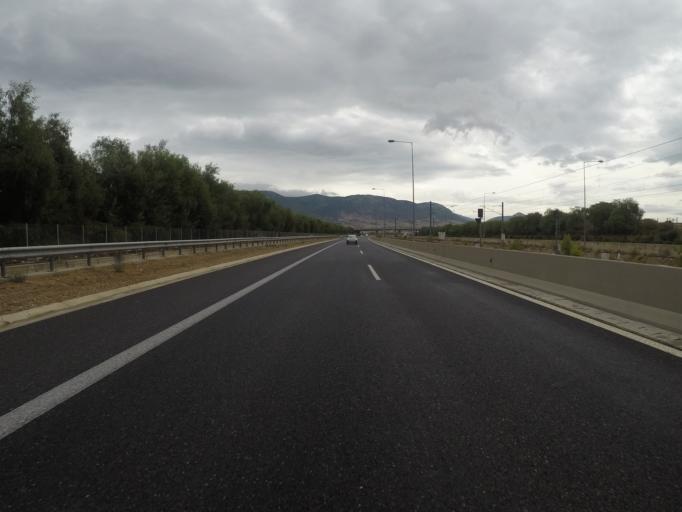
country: GR
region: Attica
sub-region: Nomarchia Dytikis Attikis
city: Magoula
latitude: 38.0896
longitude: 23.5496
